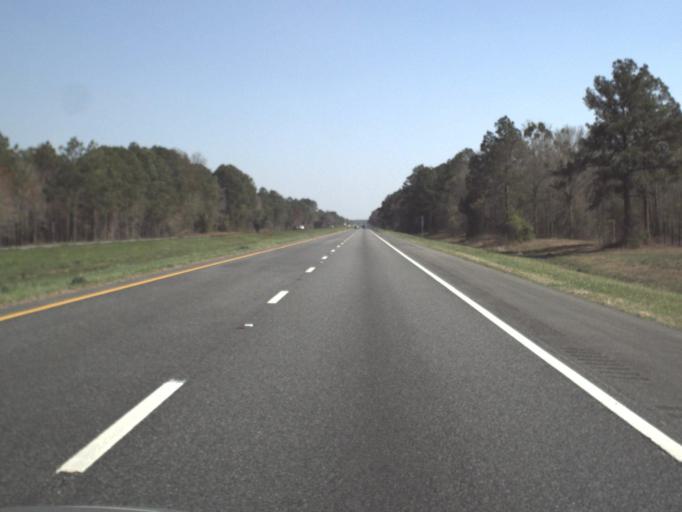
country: US
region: Florida
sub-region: Jackson County
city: Marianna
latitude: 30.7101
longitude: -85.1527
